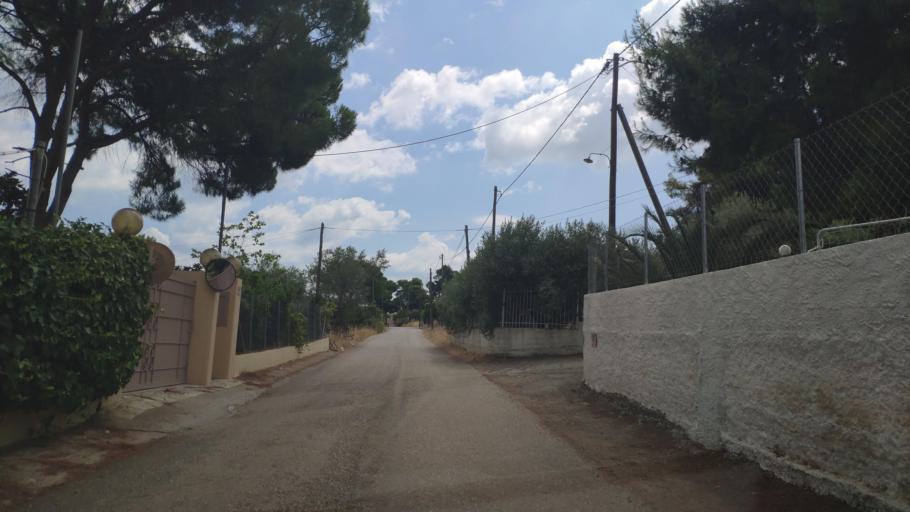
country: GR
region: Central Greece
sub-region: Nomos Fthiotidos
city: Malesina
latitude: 38.6474
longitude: 23.1951
